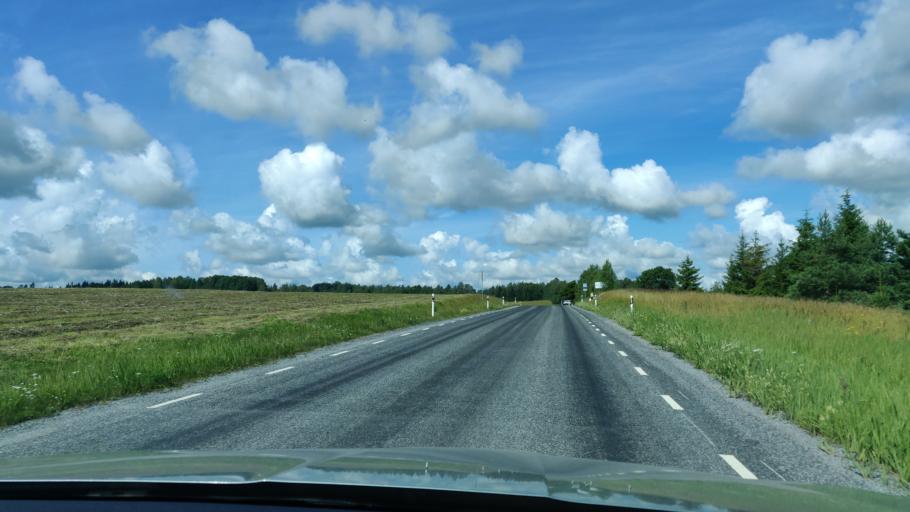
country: EE
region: Tartu
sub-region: Elva linn
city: Elva
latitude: 58.0383
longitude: 26.3576
